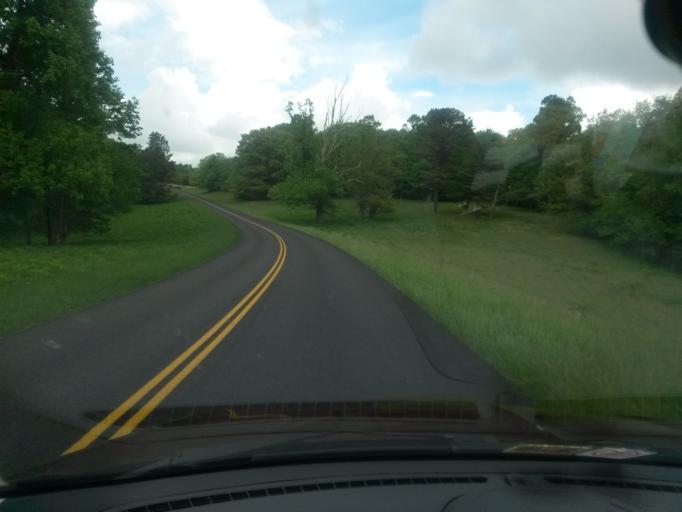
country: US
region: Virginia
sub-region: Floyd County
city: Floyd
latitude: 36.8080
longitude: -80.3526
